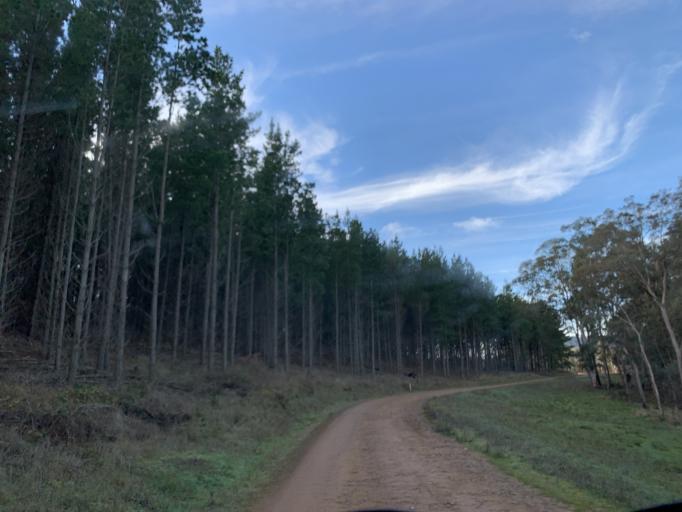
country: AU
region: Victoria
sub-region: Mansfield
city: Mansfield
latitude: -36.9237
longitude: 146.1003
